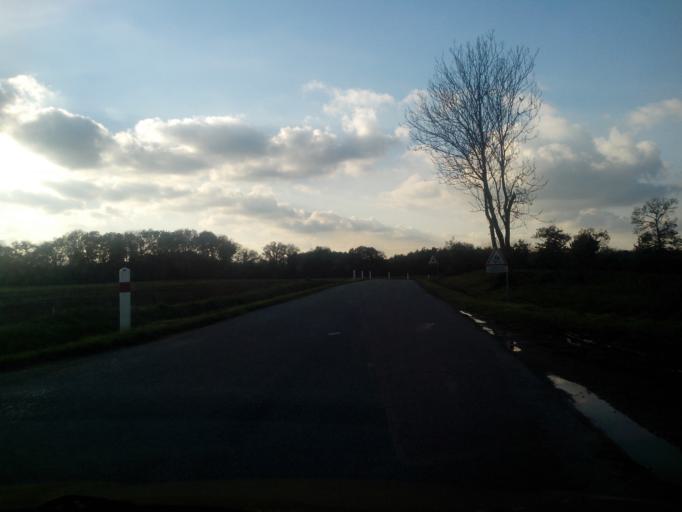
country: FR
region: Brittany
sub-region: Departement du Morbihan
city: Mauron
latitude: 48.0823
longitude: -2.3172
